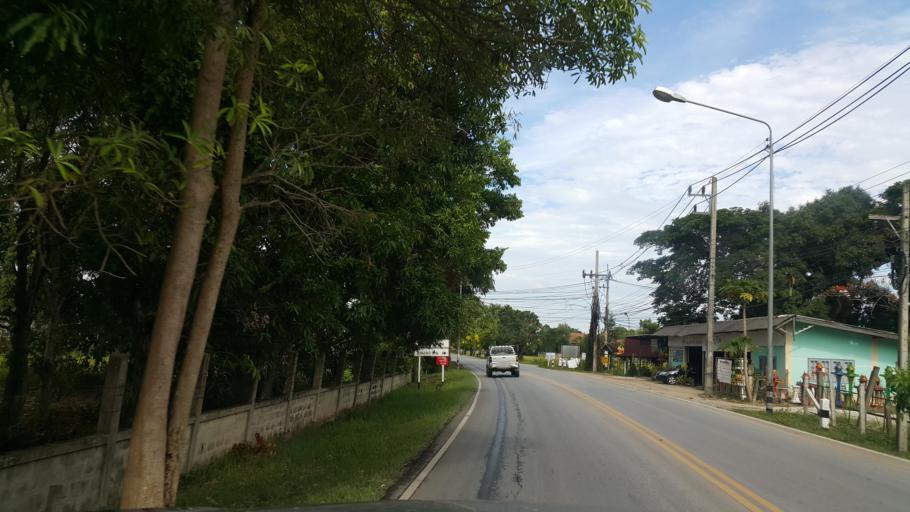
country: TH
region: Chiang Rai
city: Chiang Rai
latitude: 19.9125
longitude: 99.8724
